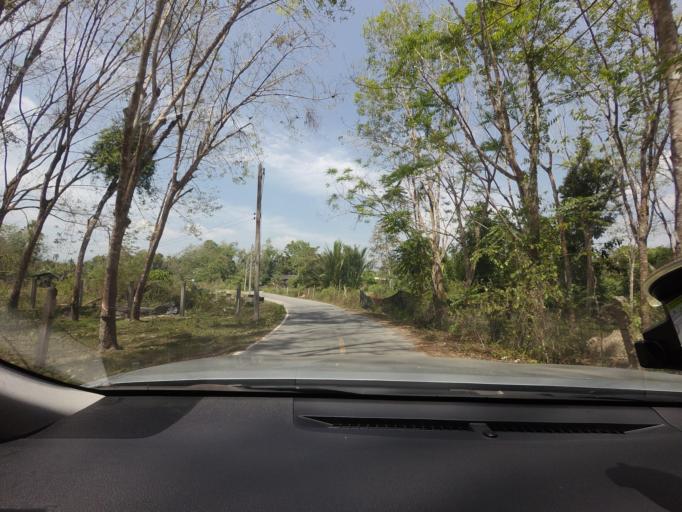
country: TH
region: Narathiwat
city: Rueso
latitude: 6.3793
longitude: 101.5030
